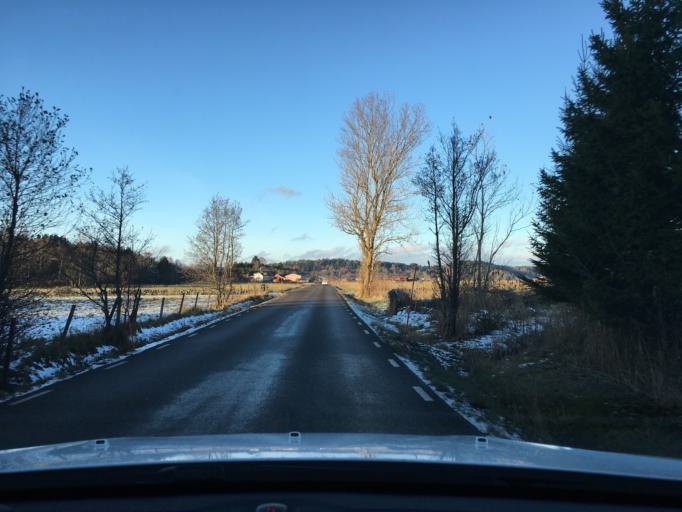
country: SE
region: Vaestra Goetaland
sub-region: Tjorns Kommun
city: Myggenas
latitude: 58.0412
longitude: 11.7326
